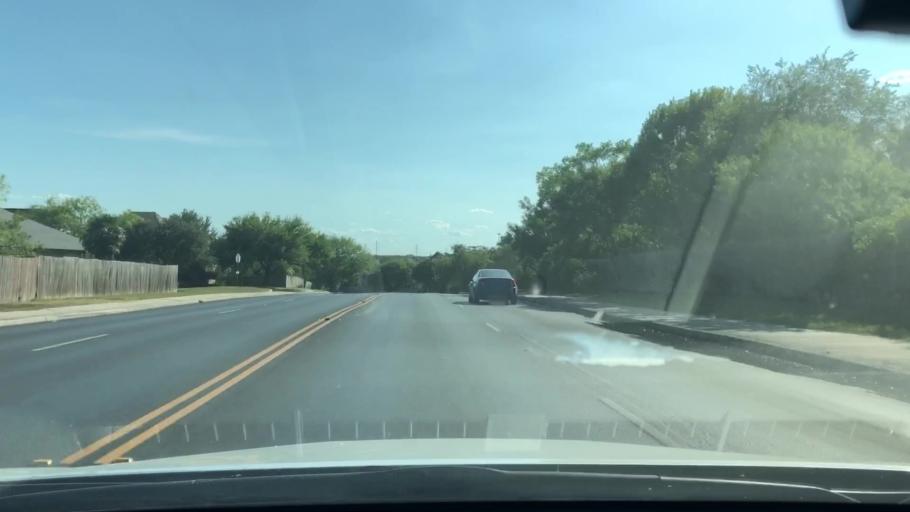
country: US
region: Texas
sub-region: Bexar County
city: Kirby
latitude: 29.4702
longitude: -98.3492
